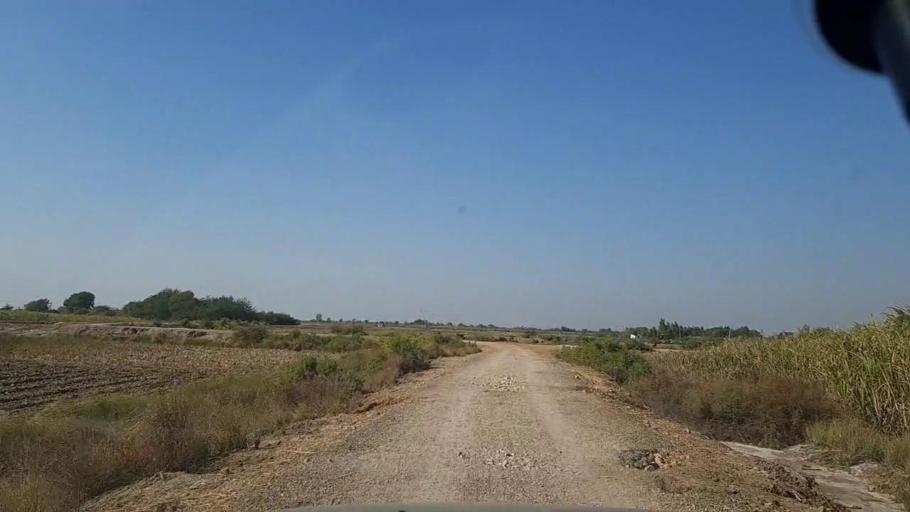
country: PK
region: Sindh
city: Chuhar Jamali
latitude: 24.5759
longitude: 68.0401
